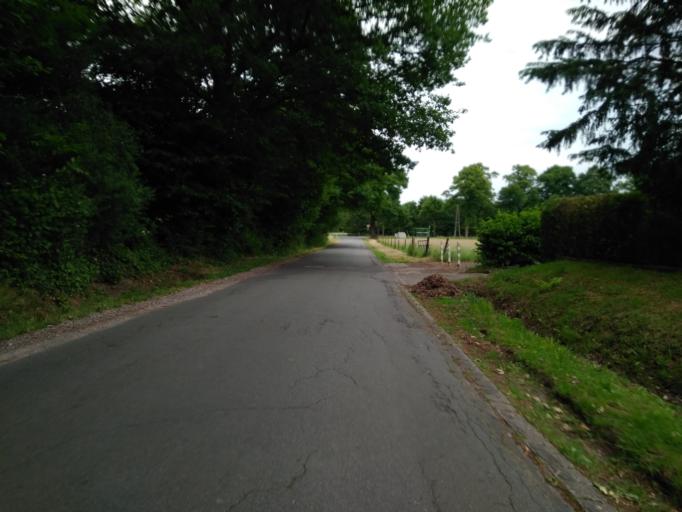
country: DE
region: North Rhine-Westphalia
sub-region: Regierungsbezirk Dusseldorf
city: Schermbeck
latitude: 51.6688
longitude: 6.8634
